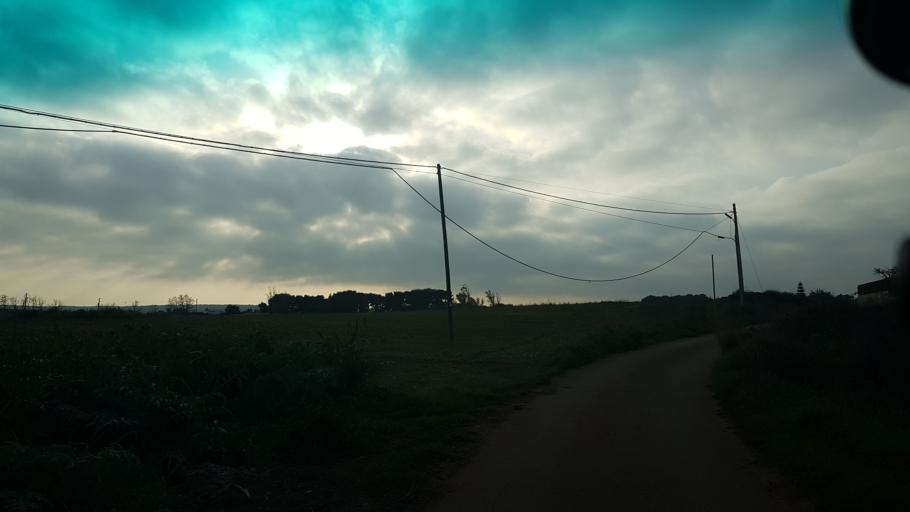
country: IT
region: Apulia
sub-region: Provincia di Brindisi
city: Carovigno
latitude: 40.7439
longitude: 17.7203
